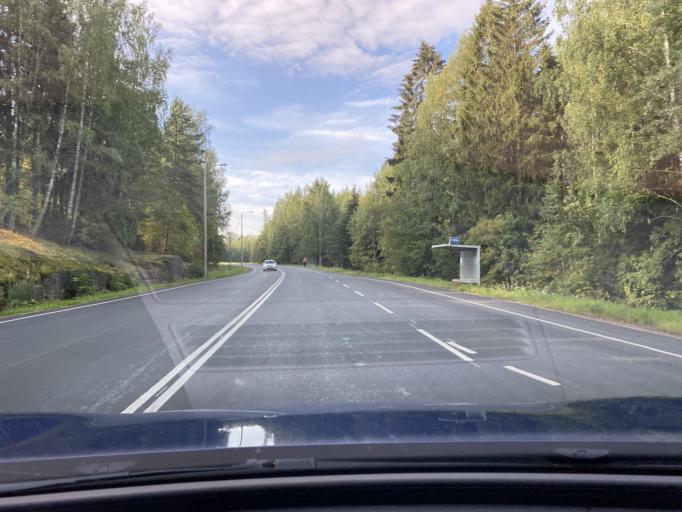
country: FI
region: Kymenlaakso
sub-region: Kouvola
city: Kouvola
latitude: 60.8834
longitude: 26.6019
